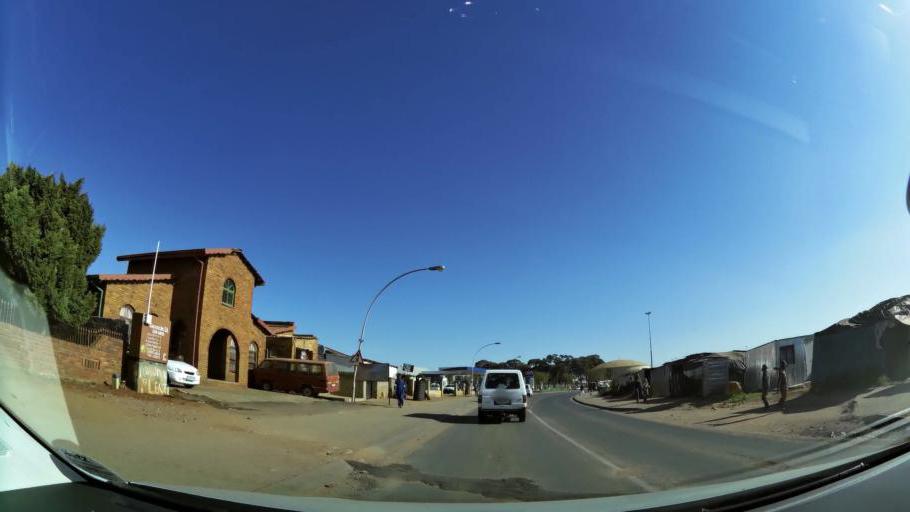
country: ZA
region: Gauteng
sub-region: Ekurhuleni Metropolitan Municipality
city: Tembisa
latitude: -26.0195
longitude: 28.2298
